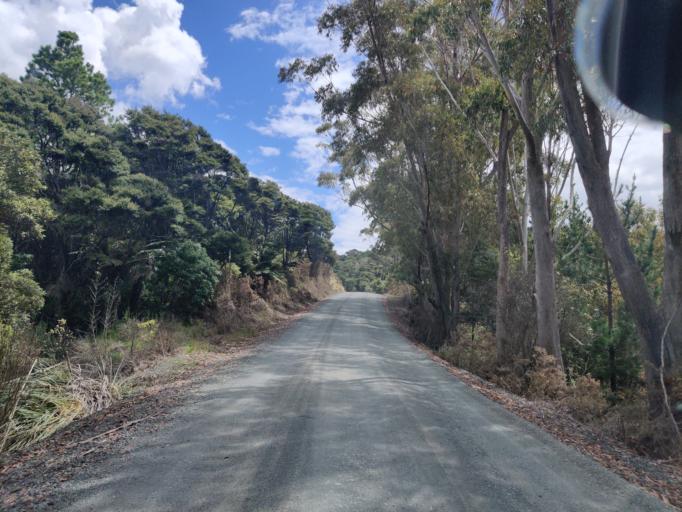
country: NZ
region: Northland
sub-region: Far North District
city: Paihia
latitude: -35.2599
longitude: 174.0519
